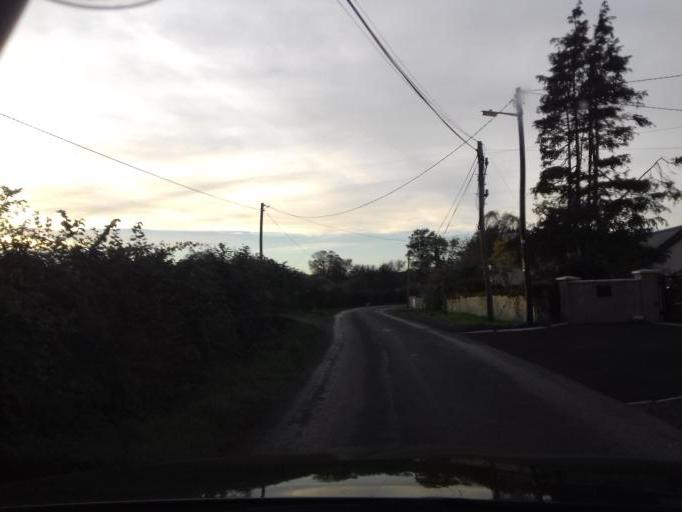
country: IE
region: Leinster
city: Hartstown
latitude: 53.3861
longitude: -6.4439
